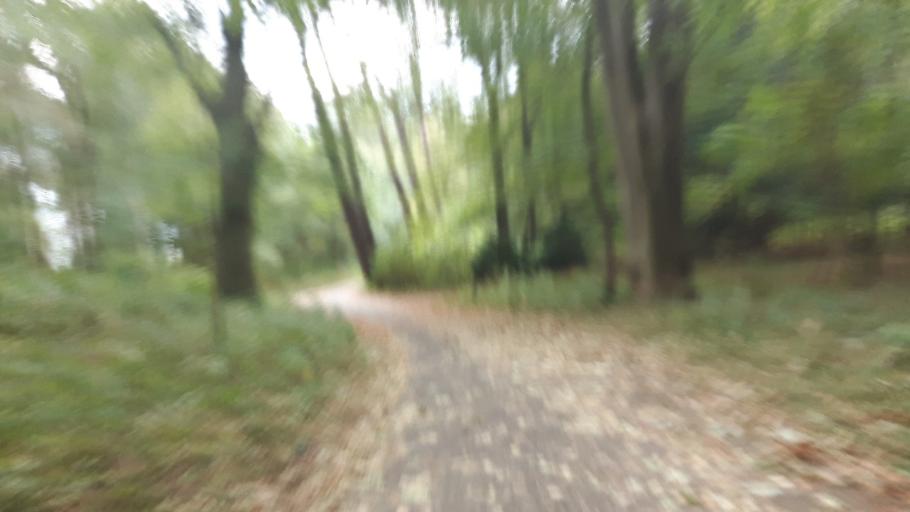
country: NL
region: North Holland
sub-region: Gemeente Bloemendaal
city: Bennebroek
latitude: 52.3361
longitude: 4.5902
